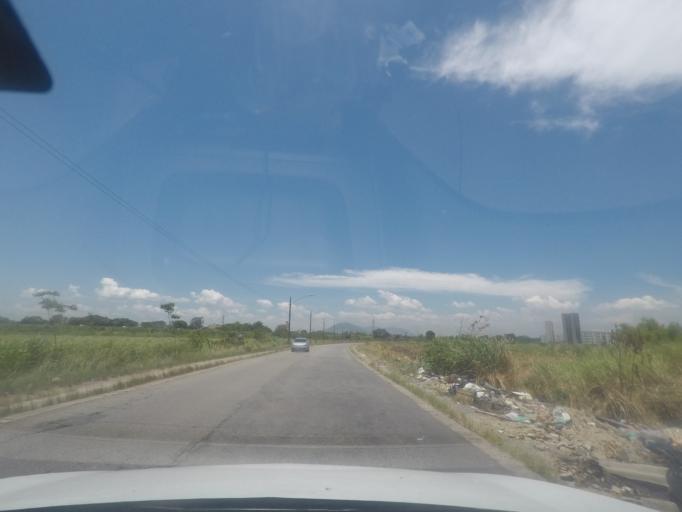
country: BR
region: Rio de Janeiro
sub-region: Itaguai
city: Itaguai
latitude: -22.8976
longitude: -43.6872
